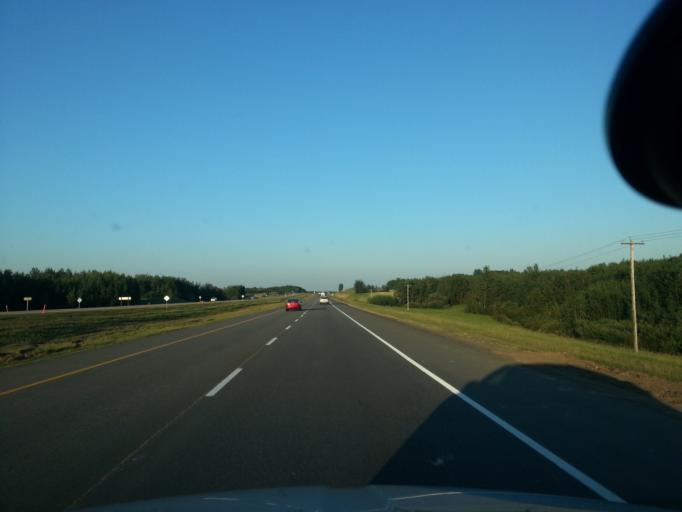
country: CA
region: Alberta
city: Stony Plain
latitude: 53.5710
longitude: -114.0952
